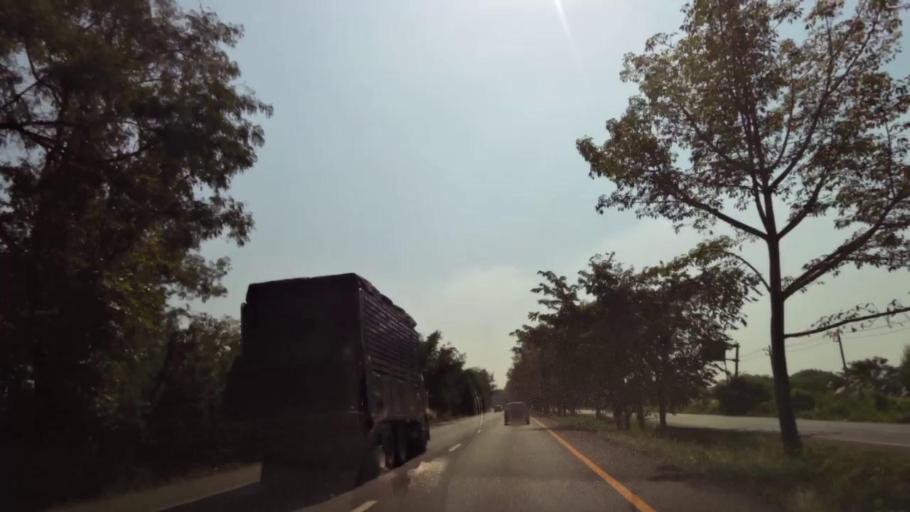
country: TH
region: Phichit
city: Bueng Na Rang
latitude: 16.0311
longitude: 100.1155
